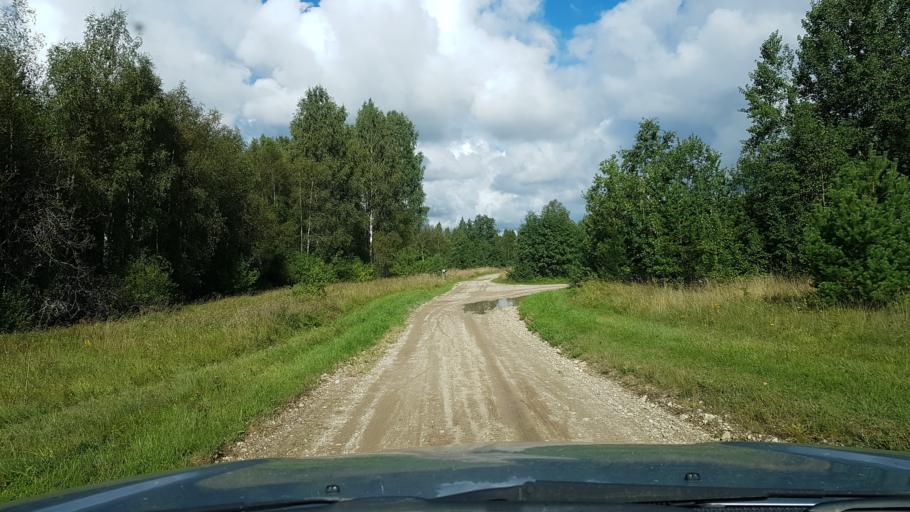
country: EE
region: Harju
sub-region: Raasiku vald
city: Arukula
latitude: 59.3110
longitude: 25.0744
